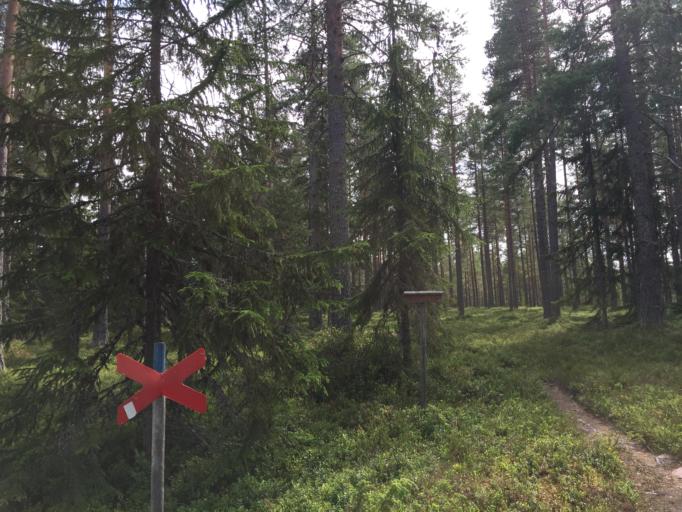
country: SE
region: Dalarna
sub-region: Malung-Saelens kommun
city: Malung
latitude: 60.6446
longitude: 13.7690
